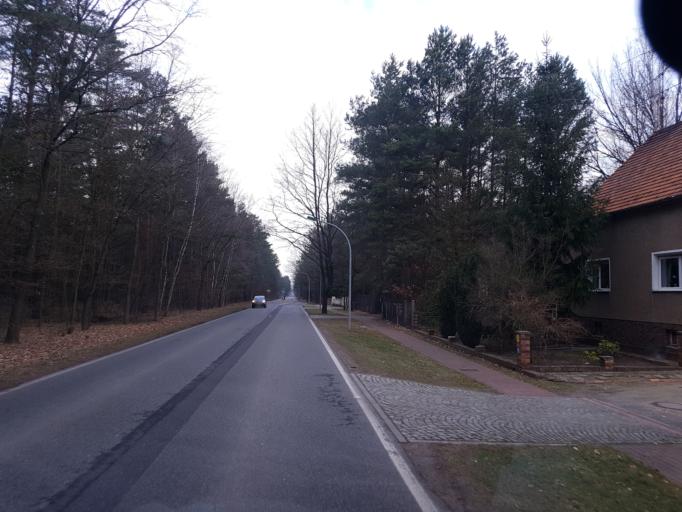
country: DE
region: Brandenburg
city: Sallgast
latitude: 51.6015
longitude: 13.7776
